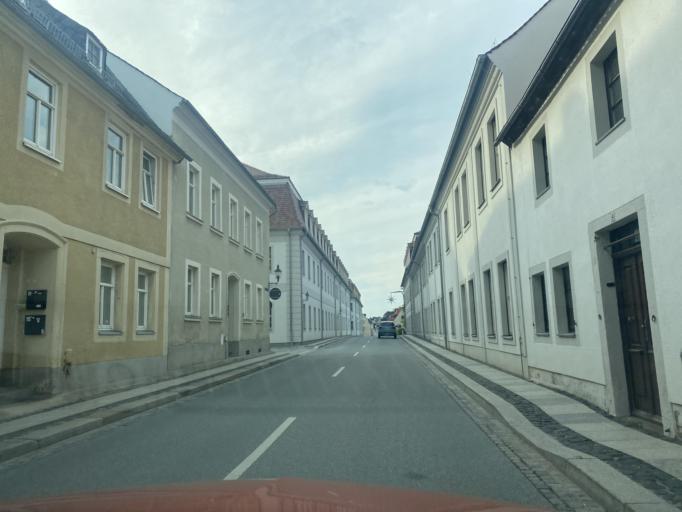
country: DE
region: Saxony
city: Herrnhut
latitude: 51.0148
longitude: 14.7449
